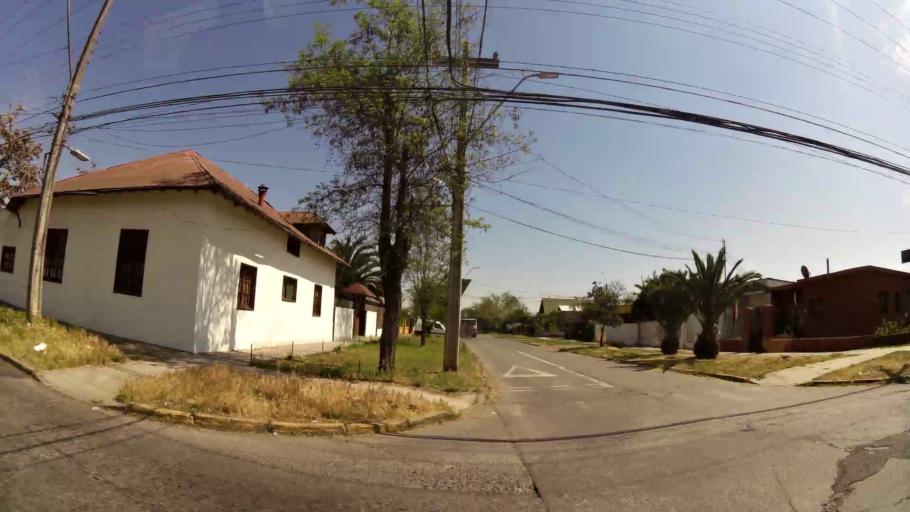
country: CL
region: Santiago Metropolitan
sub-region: Provincia de Santiago
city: La Pintana
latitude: -33.5456
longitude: -70.6637
